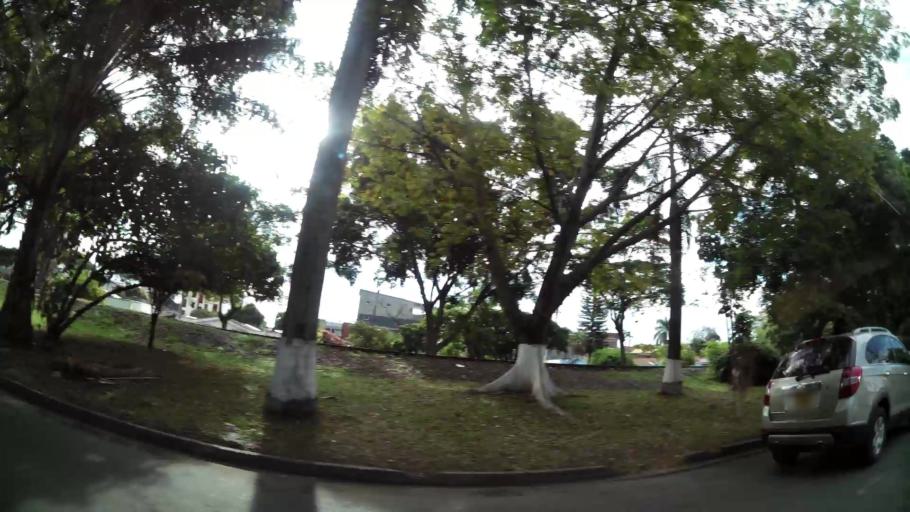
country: CO
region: Valle del Cauca
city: Cali
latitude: 3.4856
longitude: -76.5204
